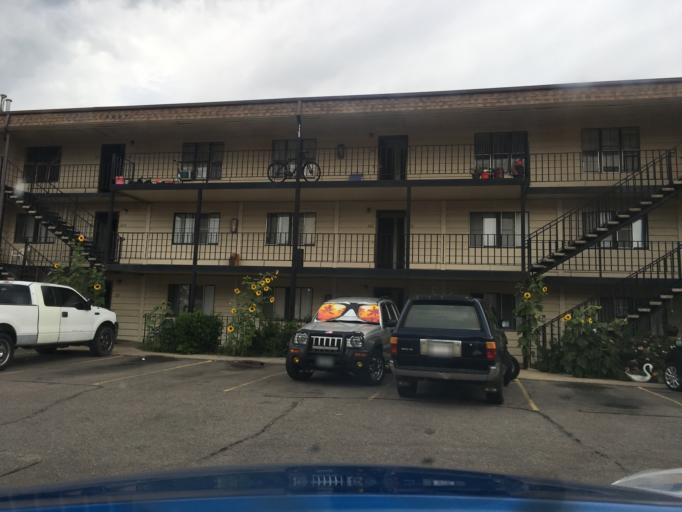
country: US
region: Colorado
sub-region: Arapahoe County
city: Sheridan
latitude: 39.6749
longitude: -105.0267
